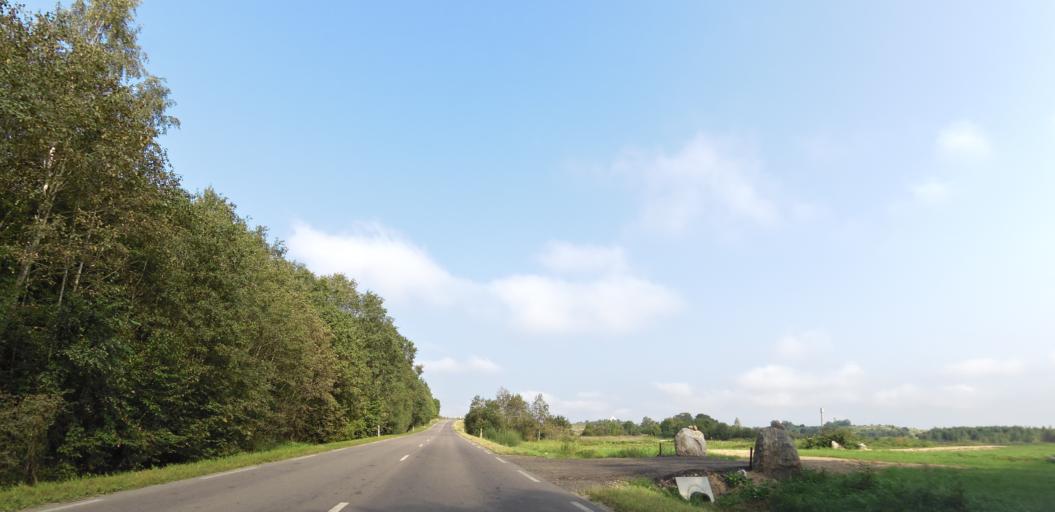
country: LT
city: Grigiskes
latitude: 54.7689
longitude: 25.0799
